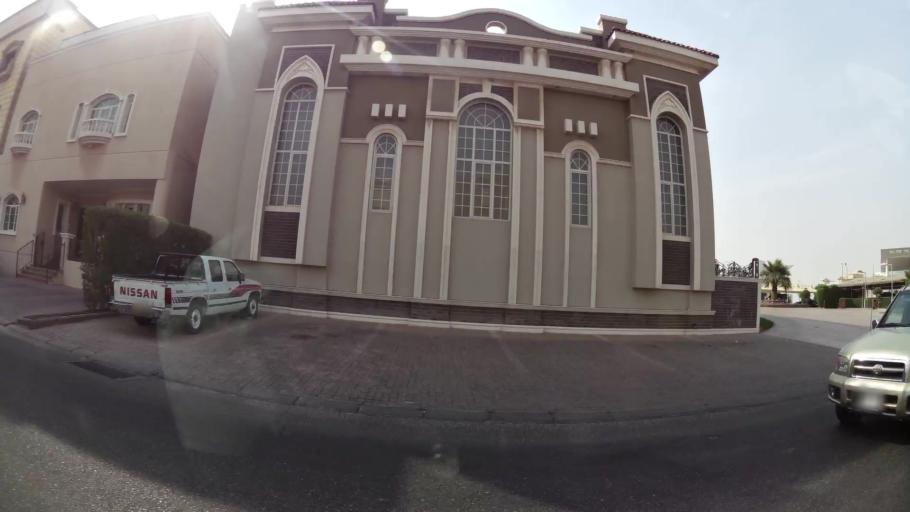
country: KW
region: Al Farwaniyah
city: Al Farwaniyah
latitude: 29.2732
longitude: 47.9392
